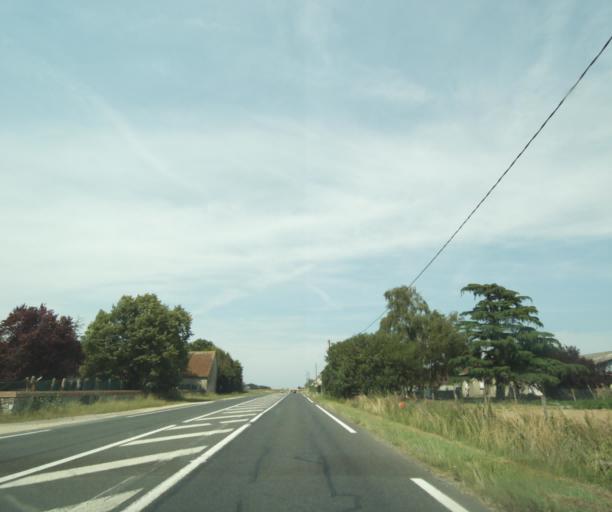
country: FR
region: Centre
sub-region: Departement d'Indre-et-Loire
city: Sainte-Maure-de-Touraine
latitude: 47.1732
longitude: 0.6552
